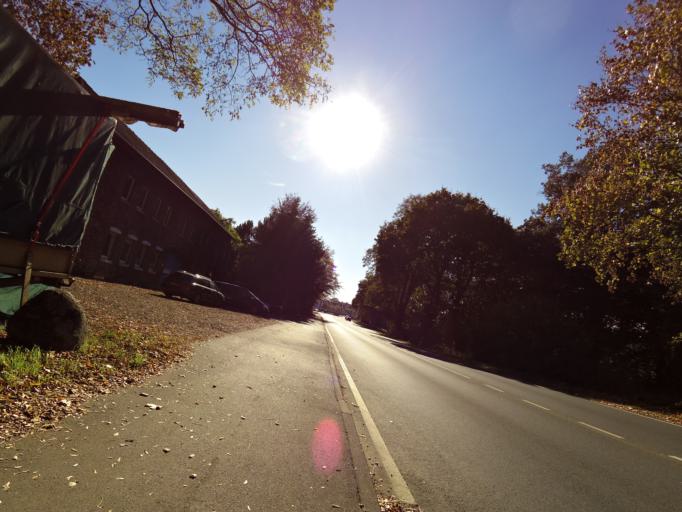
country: DE
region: North Rhine-Westphalia
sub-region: Regierungsbezirk Koln
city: Alfter
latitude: 50.7069
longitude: 7.0215
